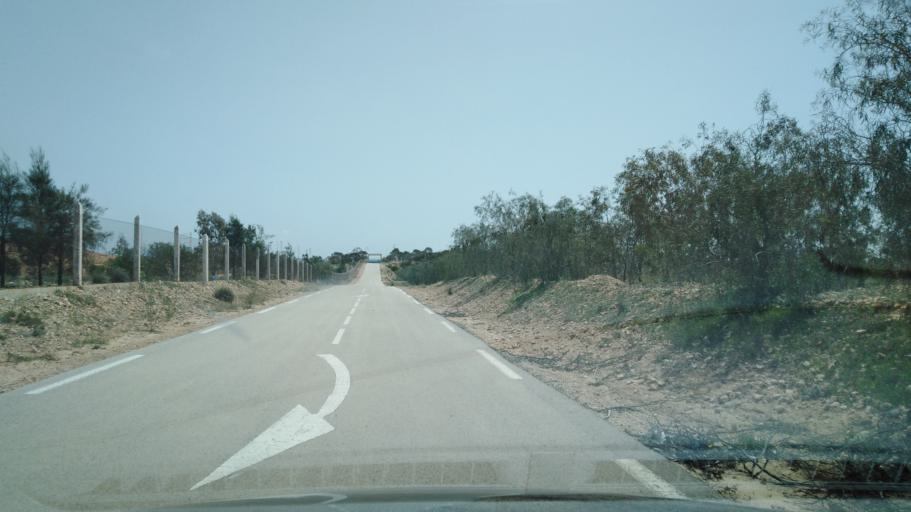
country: TN
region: Safaqis
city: Sfax
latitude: 34.7075
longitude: 10.5230
